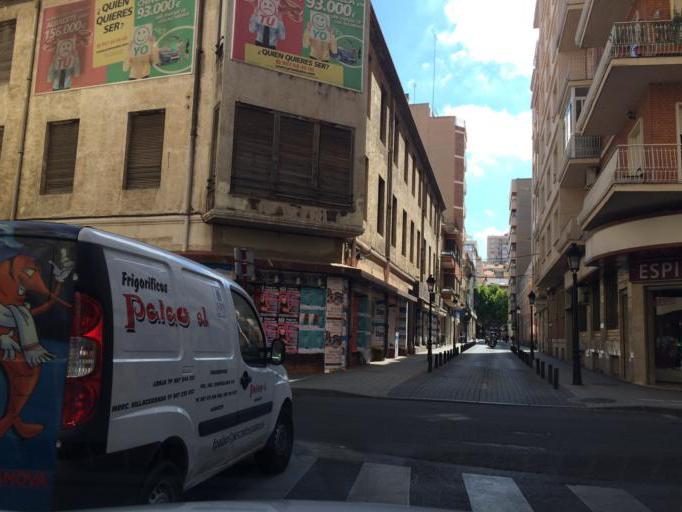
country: ES
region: Castille-La Mancha
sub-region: Provincia de Albacete
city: Albacete
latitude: 38.9968
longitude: -1.8546
